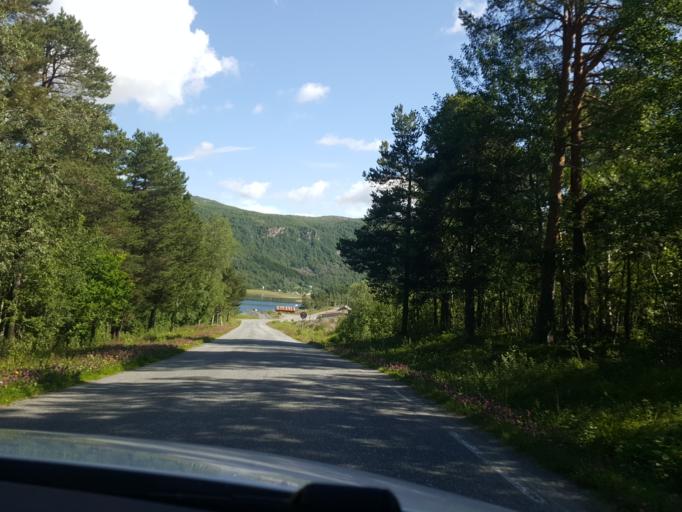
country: NO
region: Nordland
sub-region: Bodo
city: Loding
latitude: 67.1182
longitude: 14.9743
